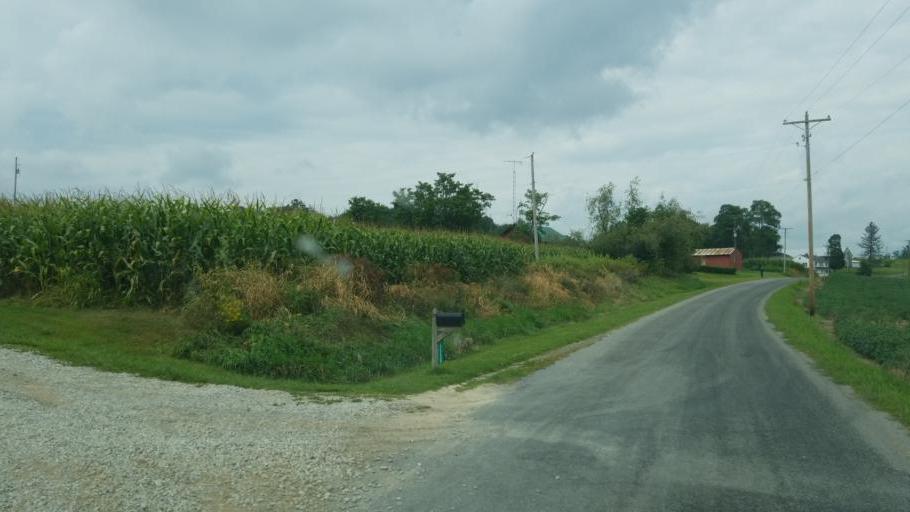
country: US
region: Ohio
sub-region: Knox County
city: Danville
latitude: 40.4846
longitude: -82.2897
